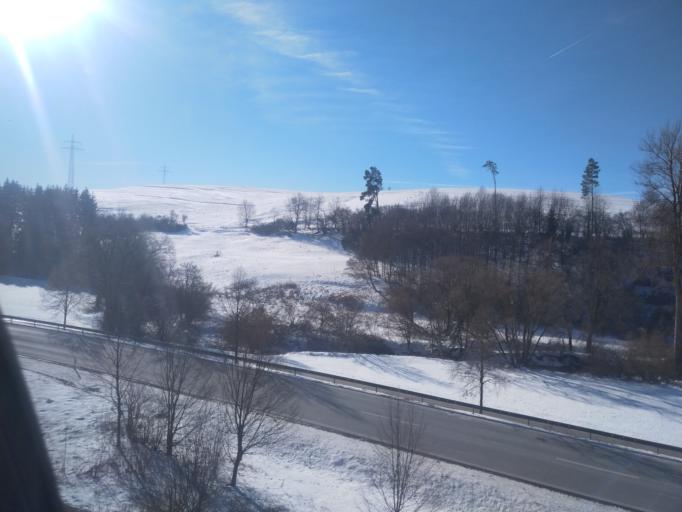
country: DE
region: Baden-Wuerttemberg
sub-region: Freiburg Region
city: Aldingen
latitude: 48.1174
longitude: 8.6865
